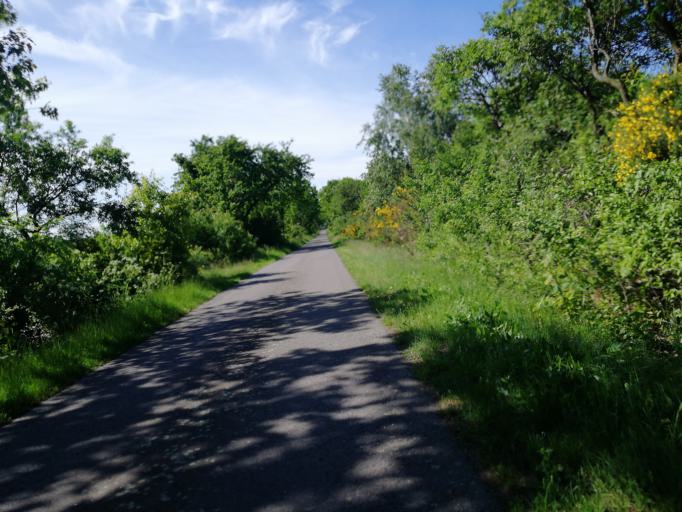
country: DE
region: Brandenburg
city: Calau
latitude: 51.7258
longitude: 13.9180
